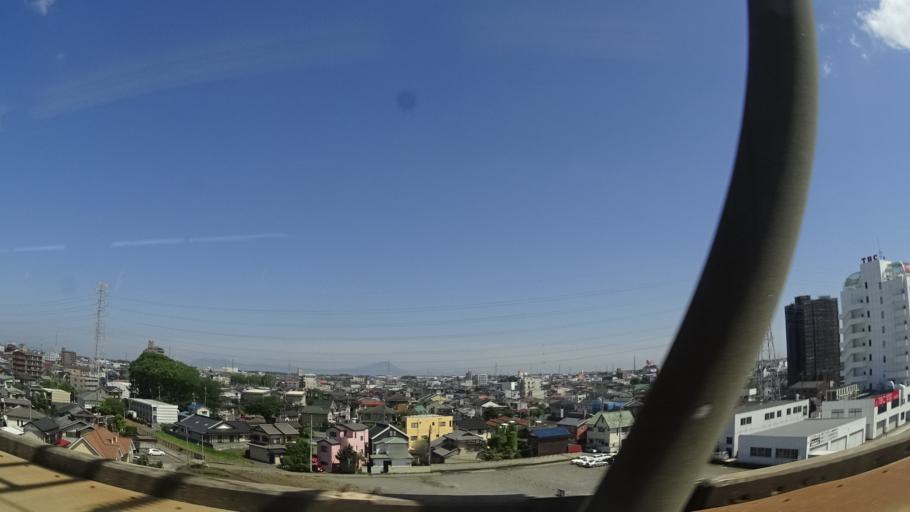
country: JP
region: Tochigi
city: Oyama
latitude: 36.3062
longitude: 139.8022
